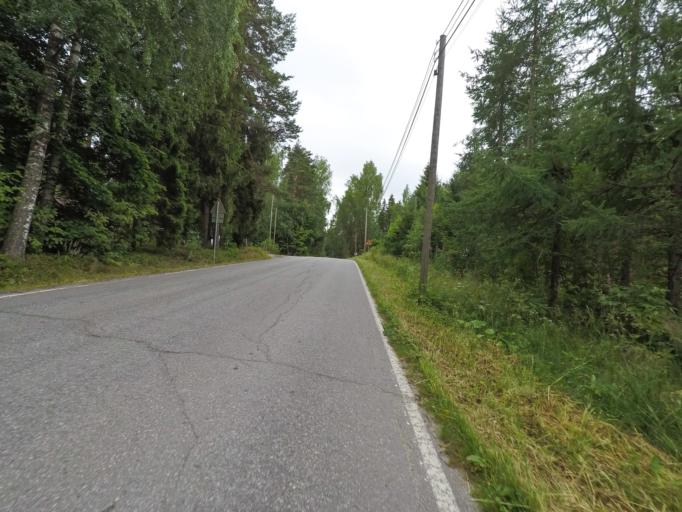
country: FI
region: Uusimaa
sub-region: Helsinki
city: Karjalohja
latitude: 60.2548
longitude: 23.7412
